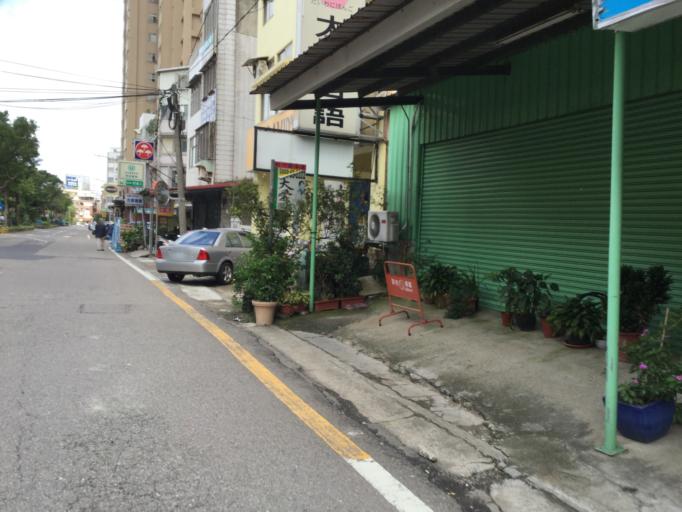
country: TW
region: Taiwan
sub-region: Hsinchu
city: Hsinchu
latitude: 24.7833
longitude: 121.0115
